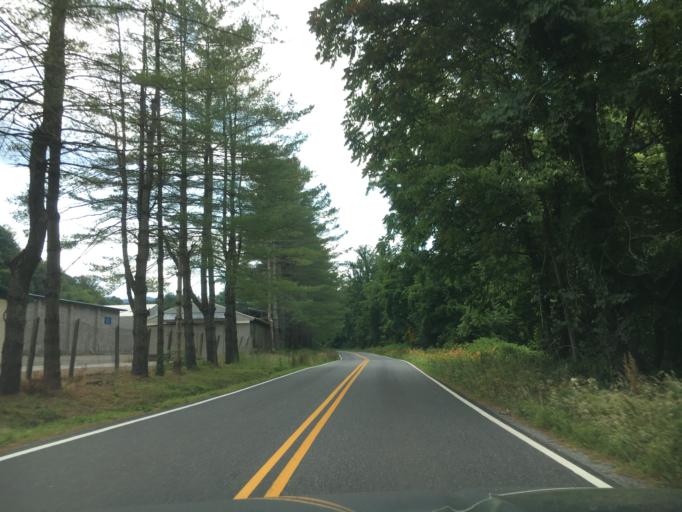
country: US
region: Virginia
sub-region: Roanoke County
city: Narrows
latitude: 37.1397
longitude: -79.9849
